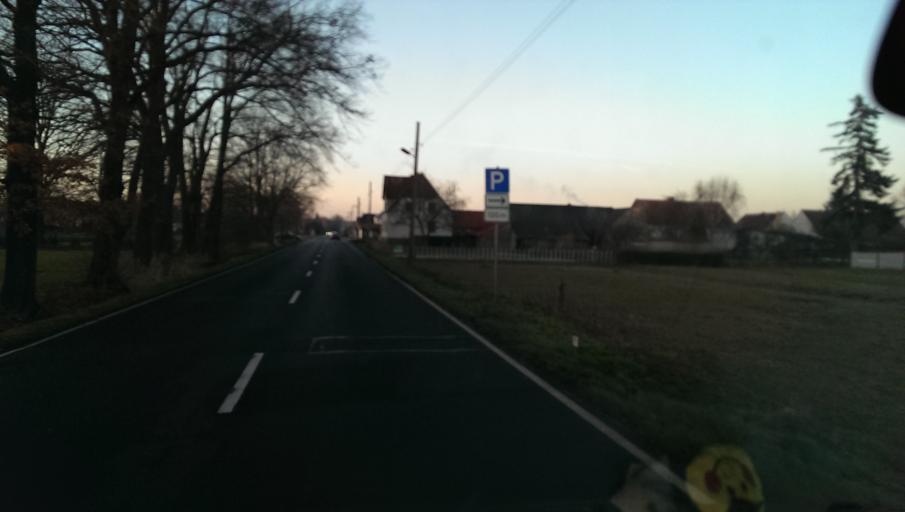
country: DE
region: Brandenburg
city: Schilda
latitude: 51.6286
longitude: 13.3210
